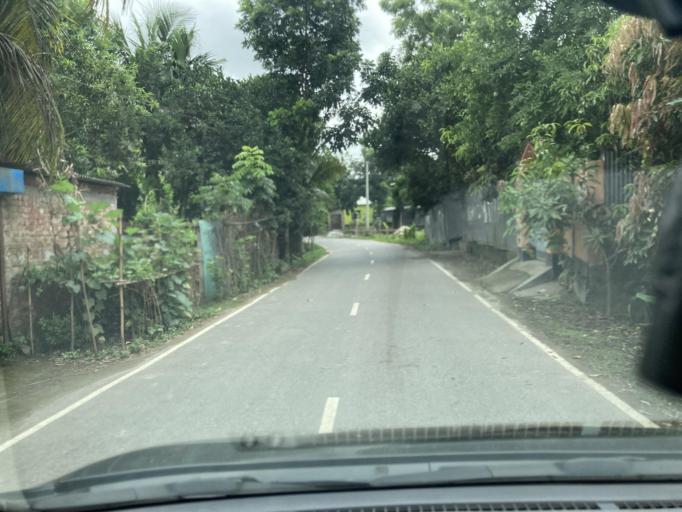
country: BD
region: Dhaka
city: Azimpur
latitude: 23.7870
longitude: 90.2167
